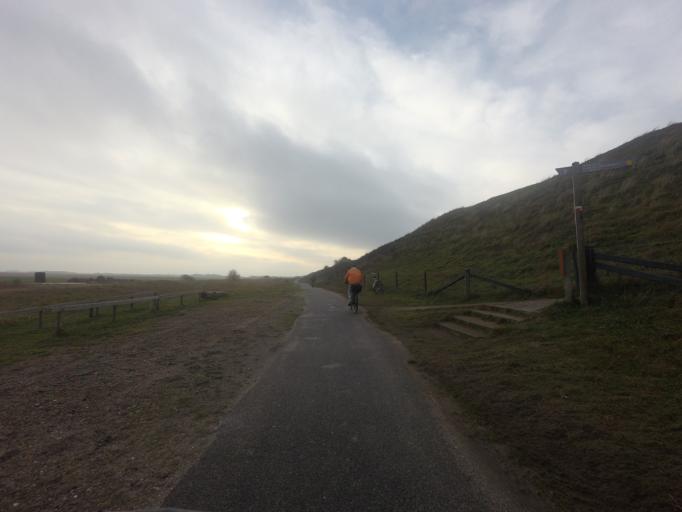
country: NL
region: North Holland
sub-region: Gemeente Texel
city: Den Burg
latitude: 53.1433
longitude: 4.8313
